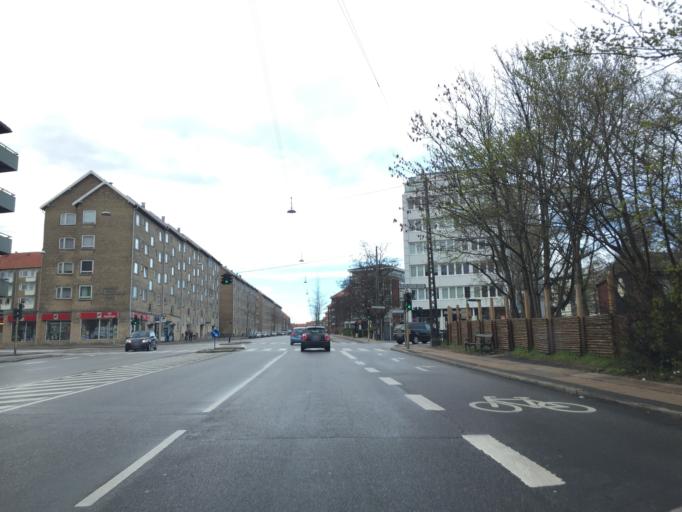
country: DK
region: Capital Region
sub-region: Frederiksberg Kommune
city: Frederiksberg
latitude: 55.7100
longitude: 12.5383
